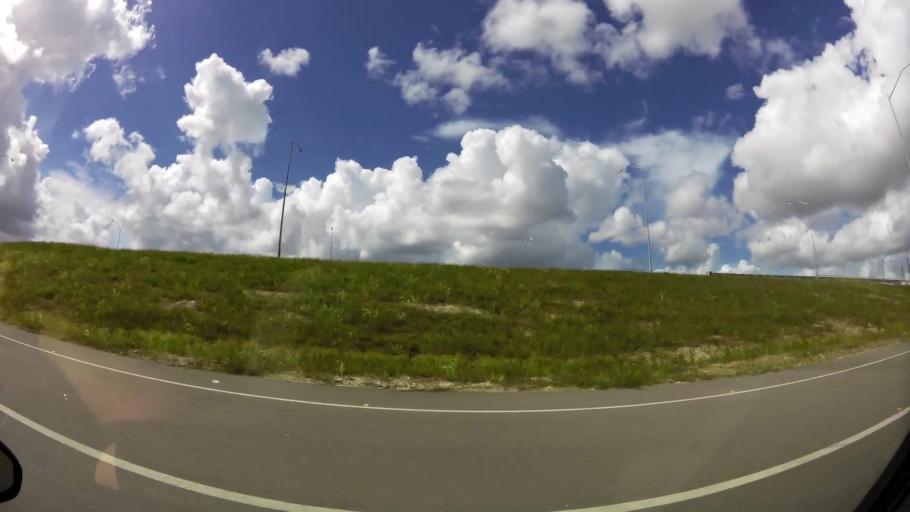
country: TT
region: Penal/Debe
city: Debe
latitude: 10.2161
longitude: -61.4554
